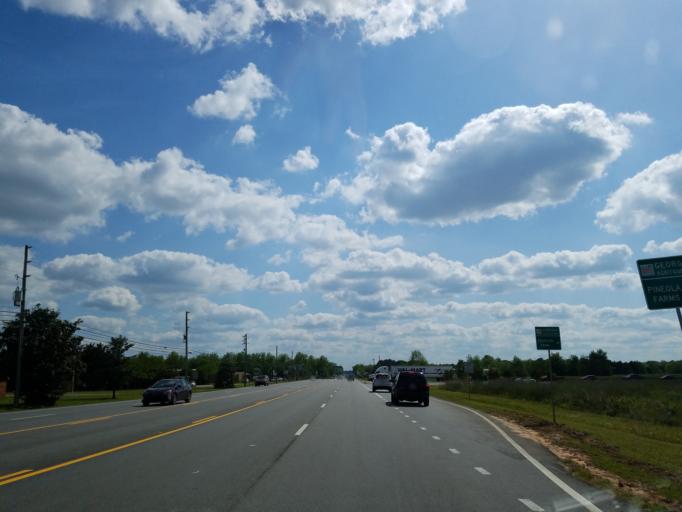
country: US
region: Georgia
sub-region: Peach County
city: Fort Valley
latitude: 32.5774
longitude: -83.8667
